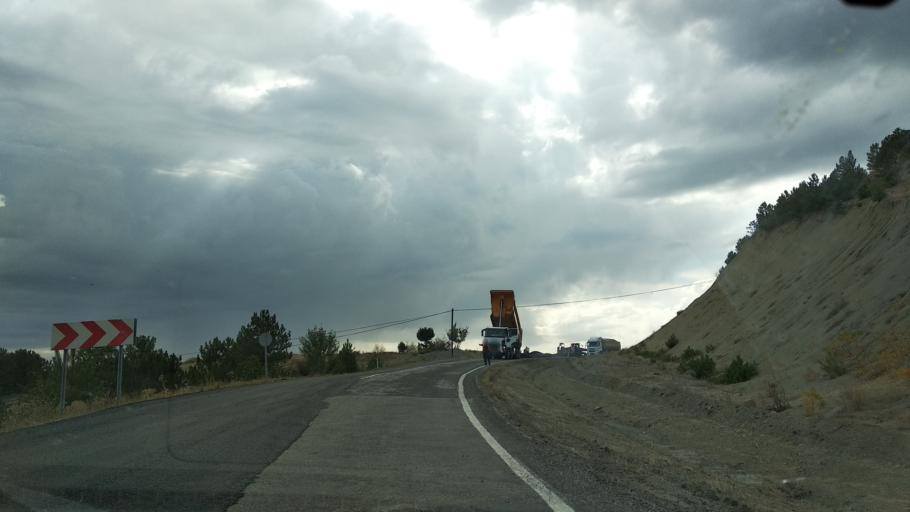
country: TR
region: Bolu
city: Seben
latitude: 40.3554
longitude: 31.4831
